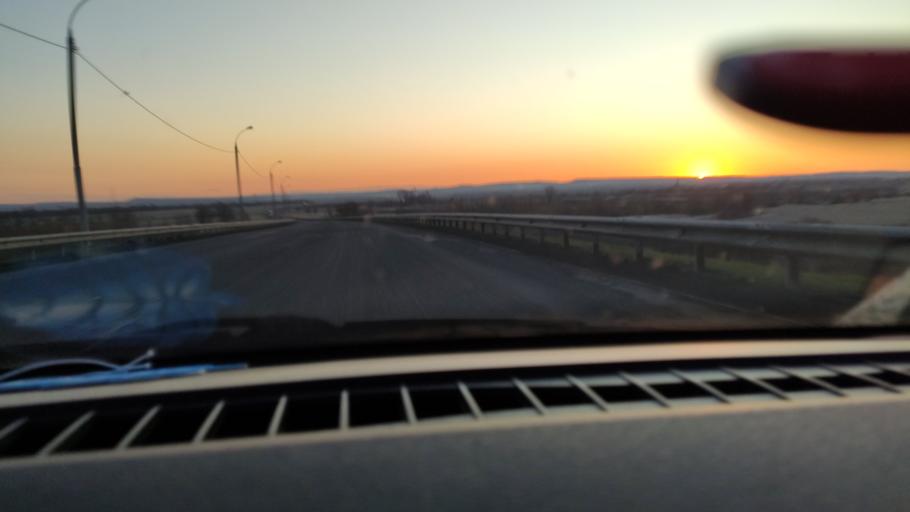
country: RU
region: Saratov
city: Yelshanka
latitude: 51.8024
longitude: 46.1894
